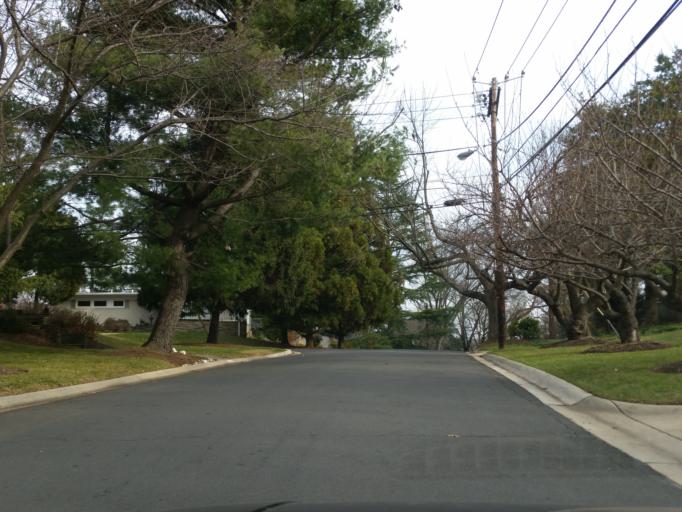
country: US
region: Maryland
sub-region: Montgomery County
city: Chevy Chase
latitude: 38.9889
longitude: -77.0681
